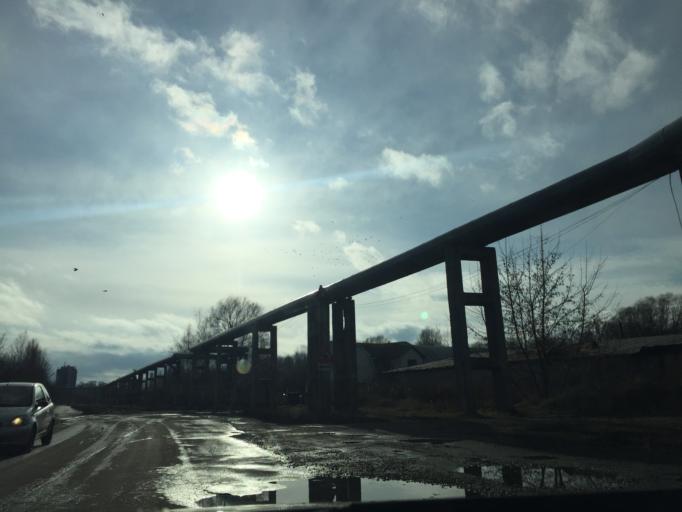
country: LV
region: Riga
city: Riga
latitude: 56.9786
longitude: 24.1065
